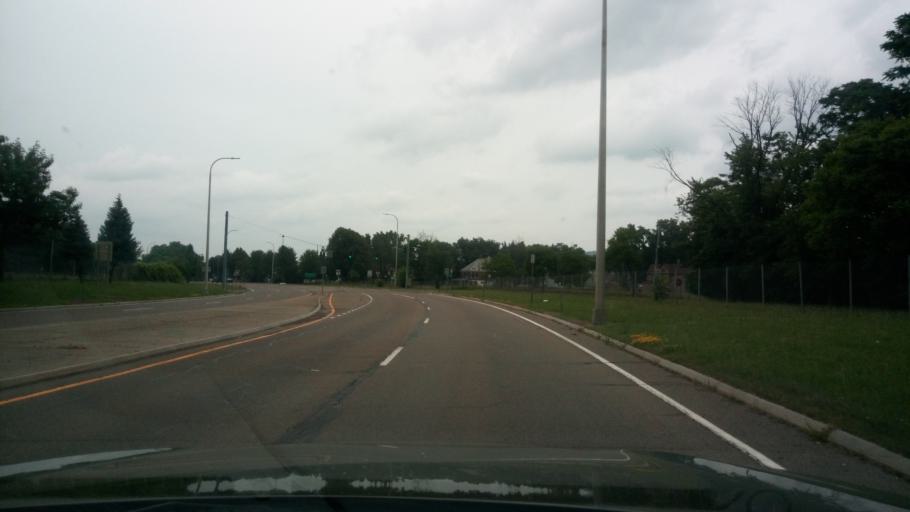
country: US
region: New York
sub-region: Chemung County
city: Elmira
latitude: 42.0802
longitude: -76.8001
